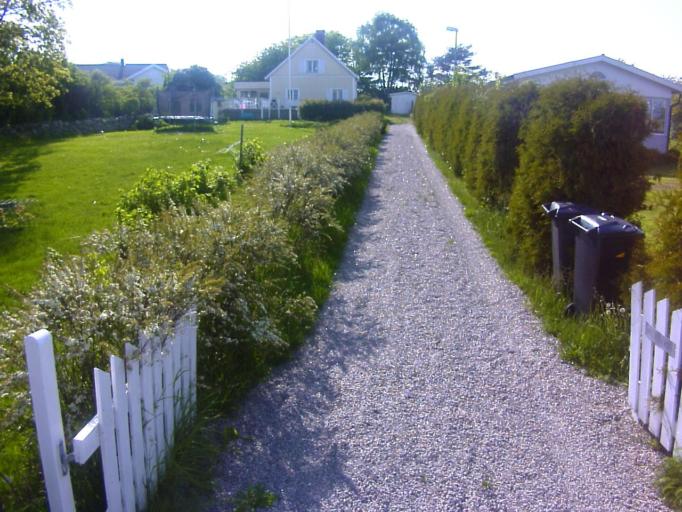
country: SE
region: Blekinge
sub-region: Karlshamns Kommun
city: Morrum
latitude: 56.0399
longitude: 14.7734
